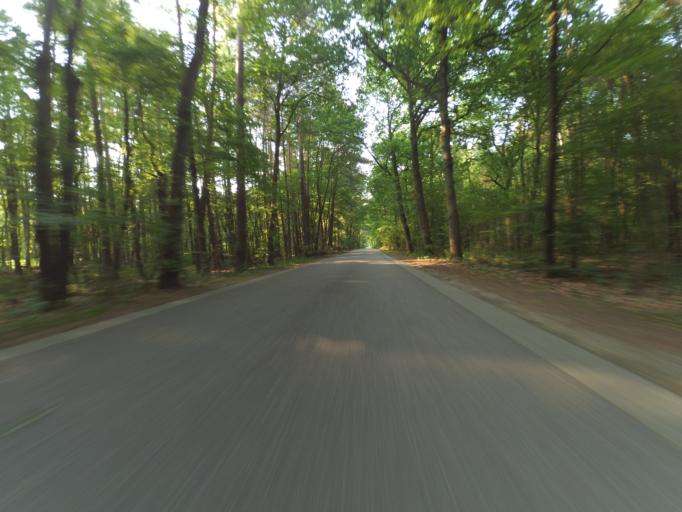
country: NL
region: Gelderland
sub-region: Gemeente Apeldoorn
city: Loenen
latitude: 52.1469
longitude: 6.0054
